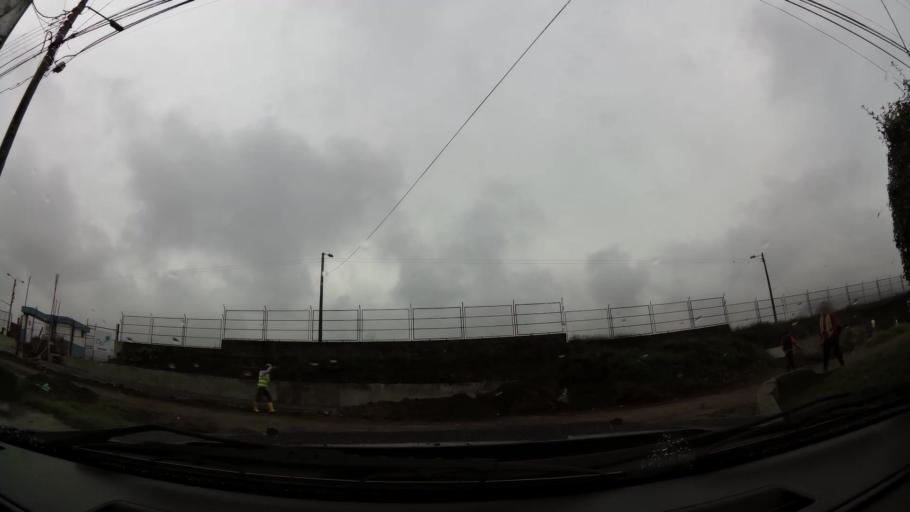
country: EC
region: Pichincha
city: Sangolqui
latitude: -0.2743
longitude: -78.4736
